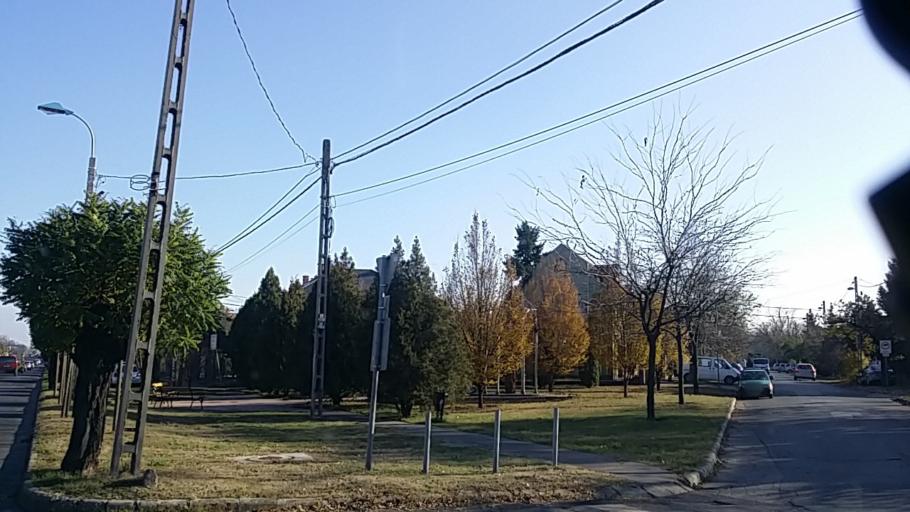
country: HU
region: Budapest
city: Budapest XVIII. keruelet
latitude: 47.4339
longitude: 19.2040
